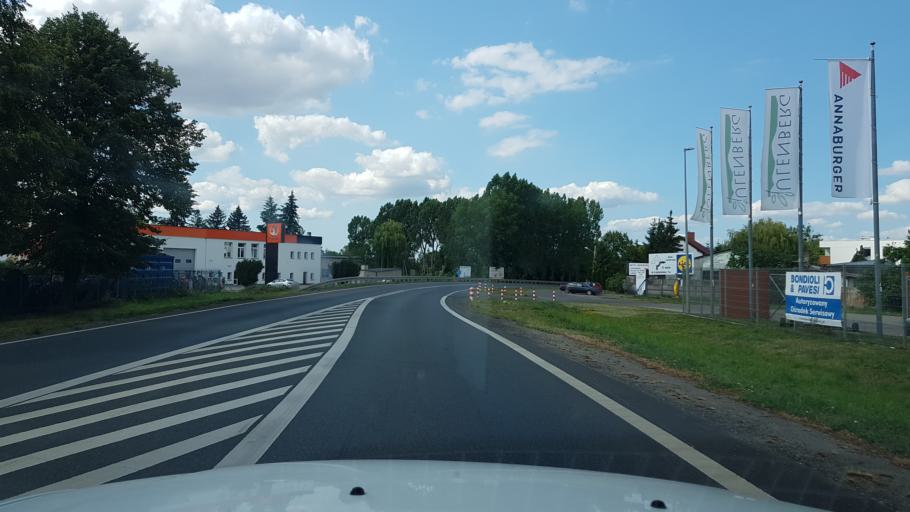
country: PL
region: West Pomeranian Voivodeship
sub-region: Powiat pyrzycki
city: Pyrzyce
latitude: 53.1266
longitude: 14.8886
